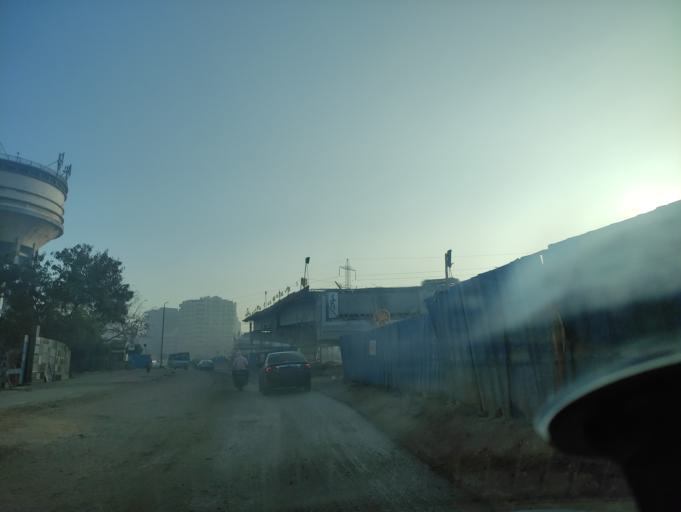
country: EG
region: Muhafazat al Qahirah
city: Cairo
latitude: 30.0475
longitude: 31.3638
